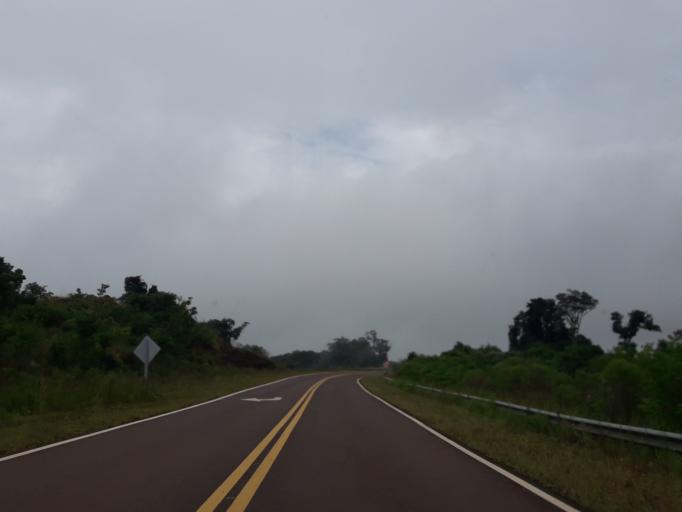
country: AR
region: Misiones
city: Bernardo de Irigoyen
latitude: -26.4055
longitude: -53.8217
